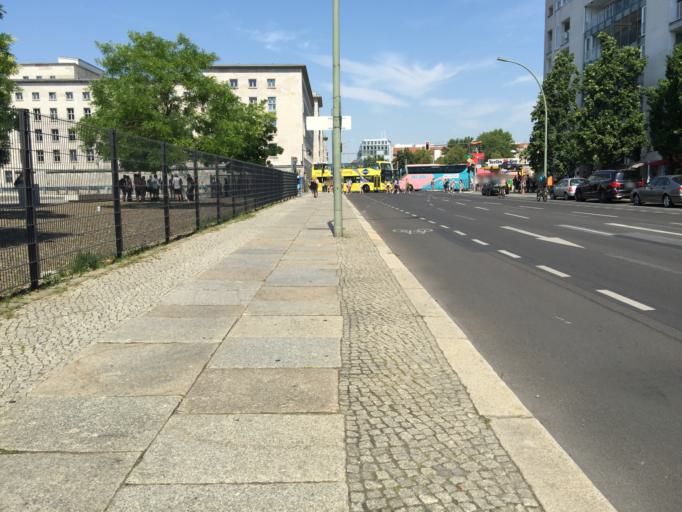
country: DE
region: Berlin
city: Bezirk Kreuzberg
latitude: 52.5066
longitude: 13.3859
